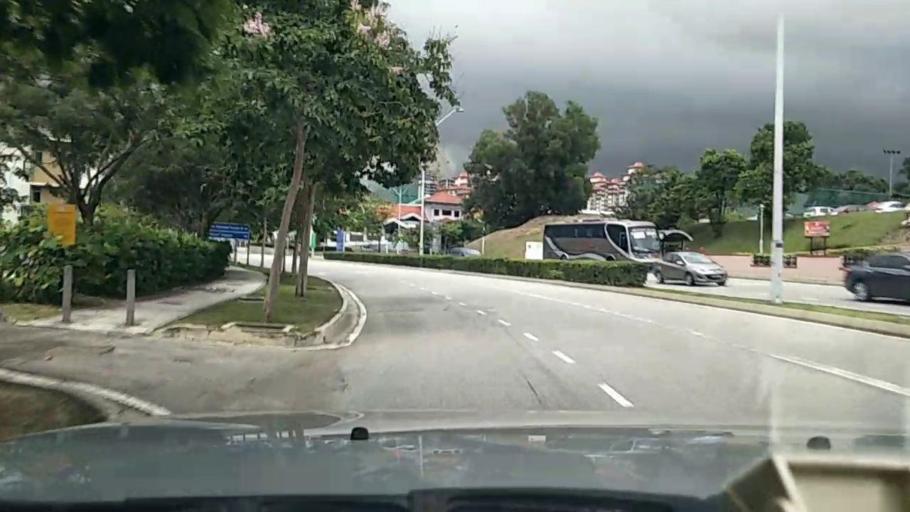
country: MY
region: Putrajaya
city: Putrajaya
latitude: 2.9324
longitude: 101.7065
